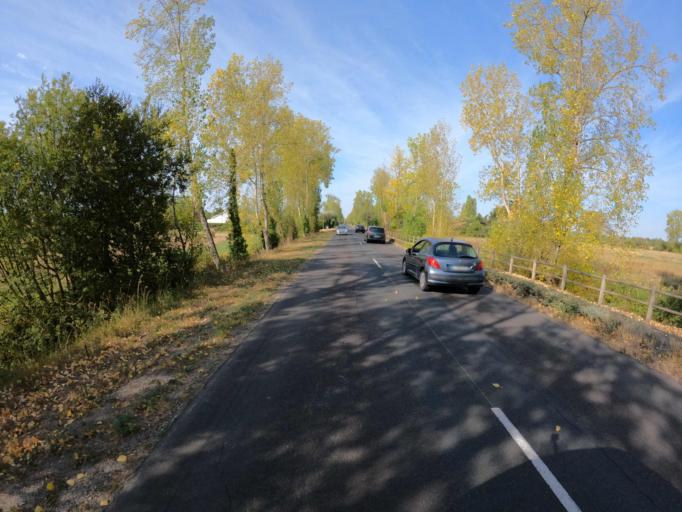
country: FR
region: Pays de la Loire
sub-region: Departement de la Vendee
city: Le Perrier
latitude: 46.8145
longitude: -2.0038
